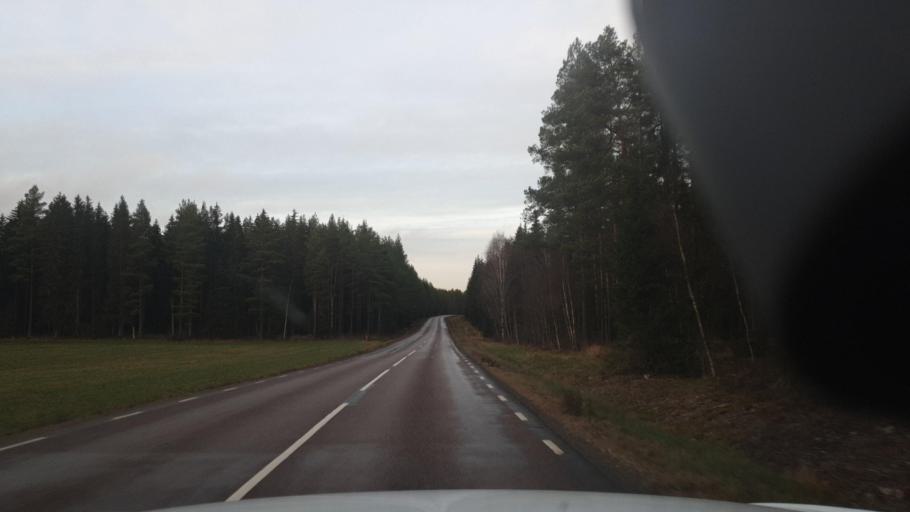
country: SE
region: Vaermland
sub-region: Eda Kommun
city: Amotfors
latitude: 59.7322
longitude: 12.1706
